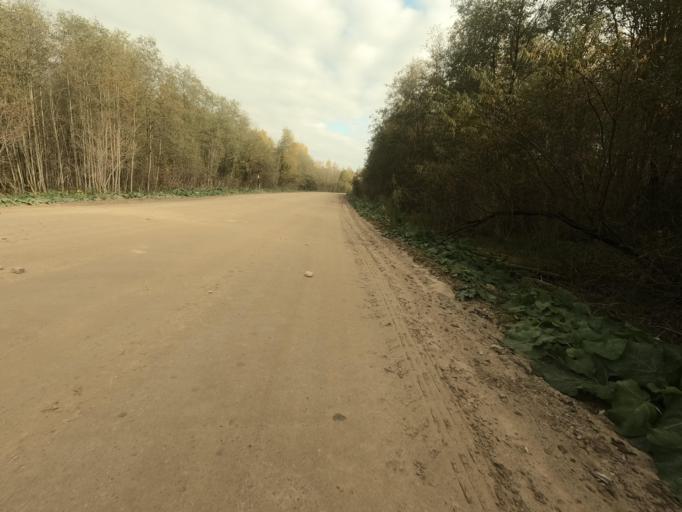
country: RU
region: Novgorod
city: Batetskiy
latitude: 58.8011
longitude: 30.6426
